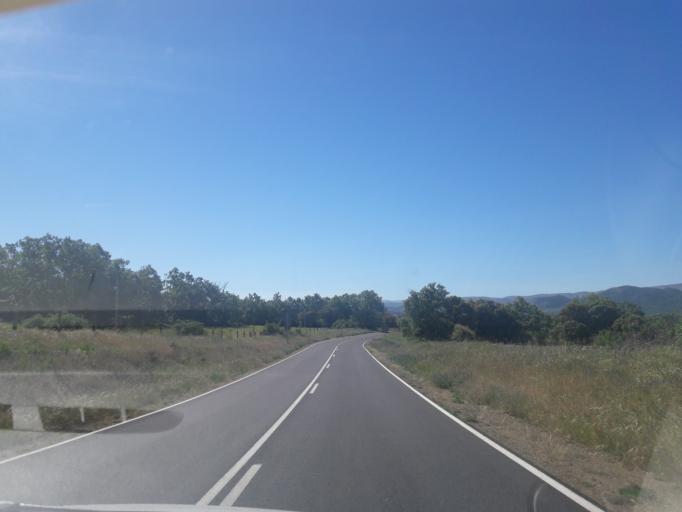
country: ES
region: Castille and Leon
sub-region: Provincia de Salamanca
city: Nava de Bejar
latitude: 40.4885
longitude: -5.6553
